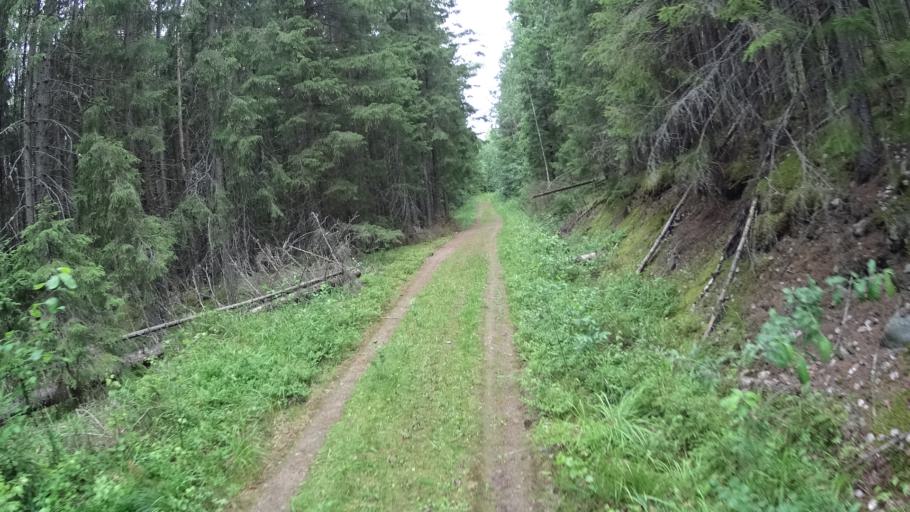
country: FI
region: Southern Savonia
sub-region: Mikkeli
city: Maentyharju
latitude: 61.1865
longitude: 26.8279
